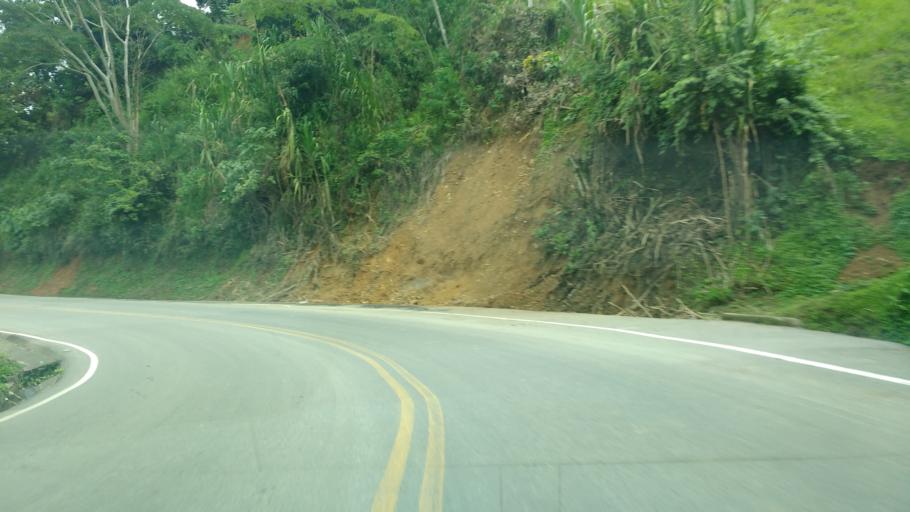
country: CO
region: Antioquia
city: Titiribi
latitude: 6.0616
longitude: -75.7459
